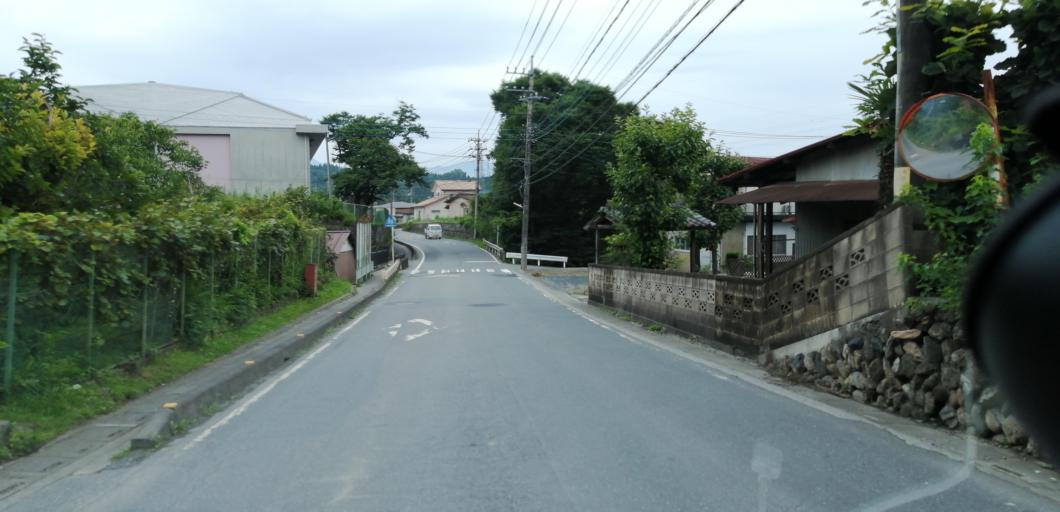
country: JP
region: Saitama
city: Chichibu
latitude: 36.0225
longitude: 139.1151
